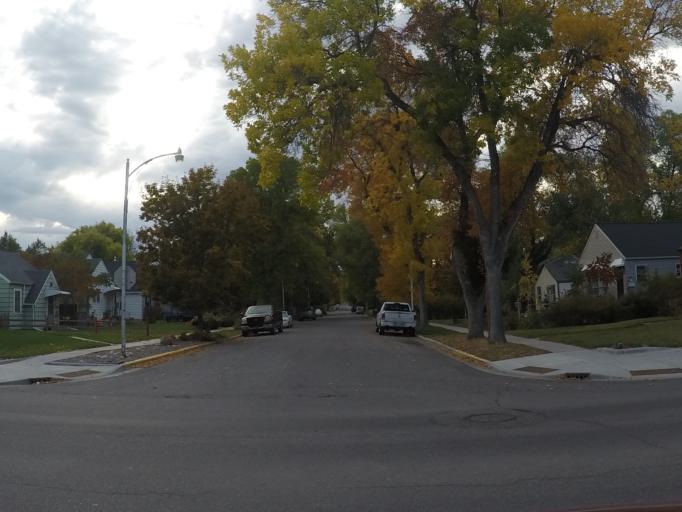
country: US
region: Montana
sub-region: Yellowstone County
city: Billings
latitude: 45.7821
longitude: -108.5280
